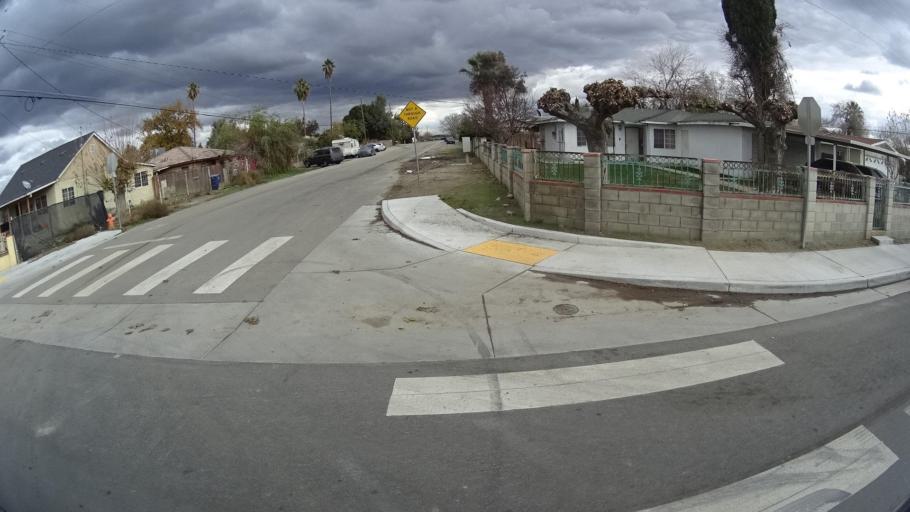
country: US
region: California
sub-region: Kern County
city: Greenfield
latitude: 35.3067
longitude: -118.9942
